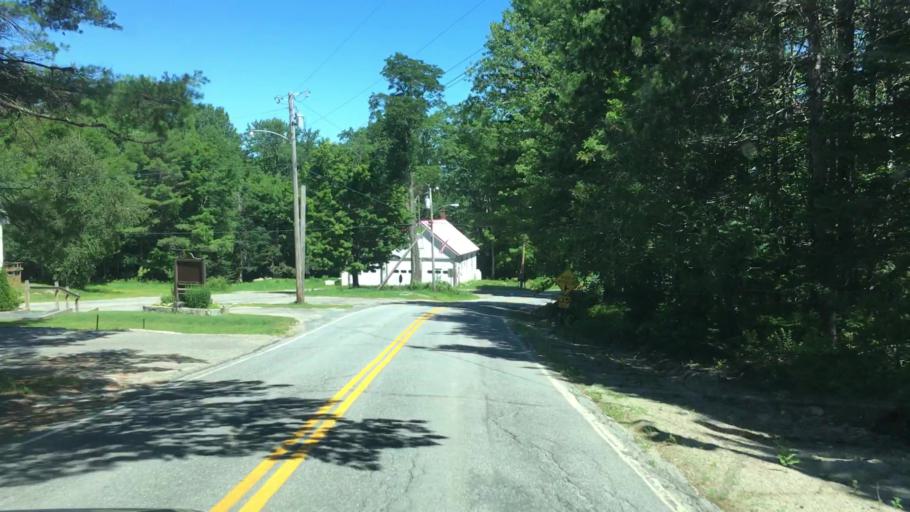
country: US
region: Maine
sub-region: Hancock County
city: Penobscot
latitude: 44.4501
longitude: -68.7027
